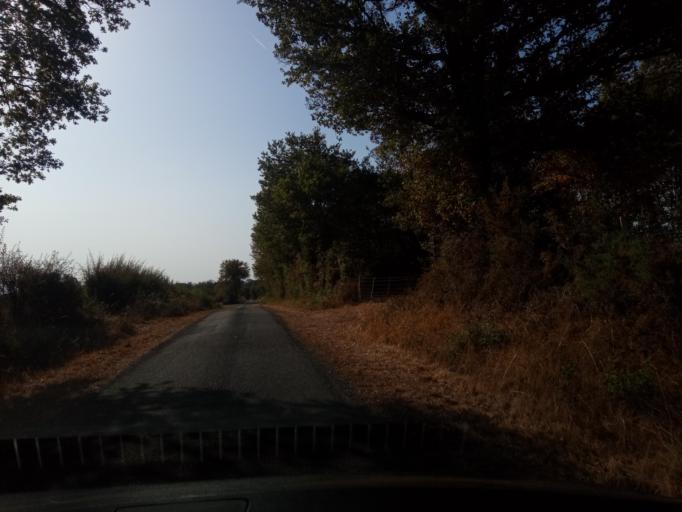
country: FR
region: Poitou-Charentes
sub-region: Departement de la Vienne
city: Saulge
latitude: 46.3743
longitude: 0.8625
